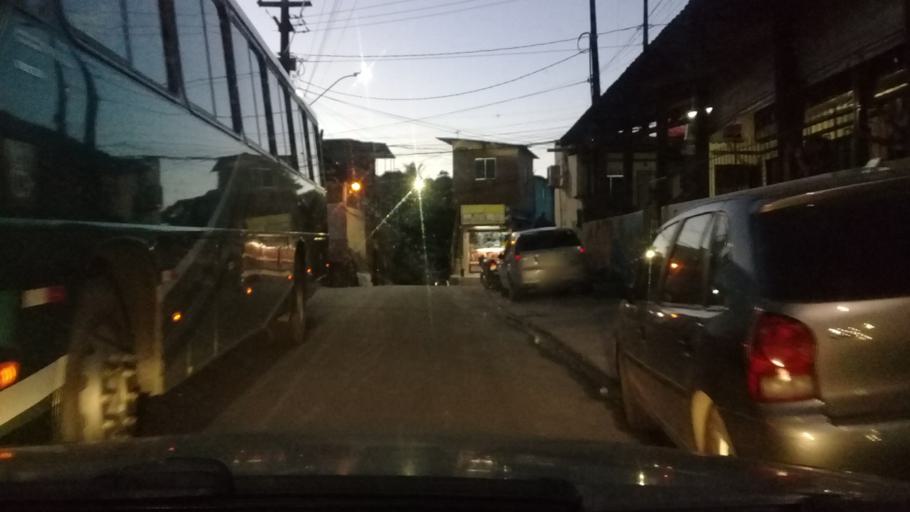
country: BR
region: Pernambuco
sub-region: Jaboatao Dos Guararapes
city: Jaboatao dos Guararapes
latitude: -8.1118
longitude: -34.9538
